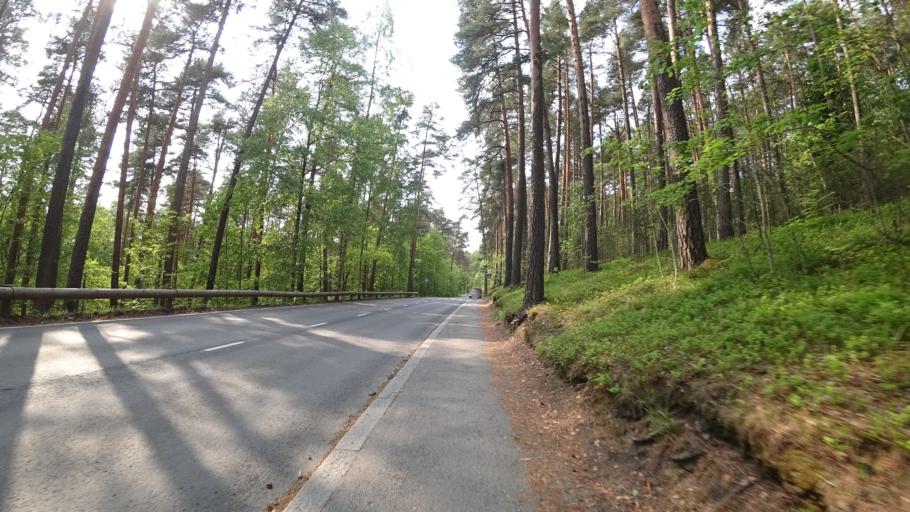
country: FI
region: Pirkanmaa
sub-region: Tampere
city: Tampere
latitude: 61.4937
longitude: 23.7368
